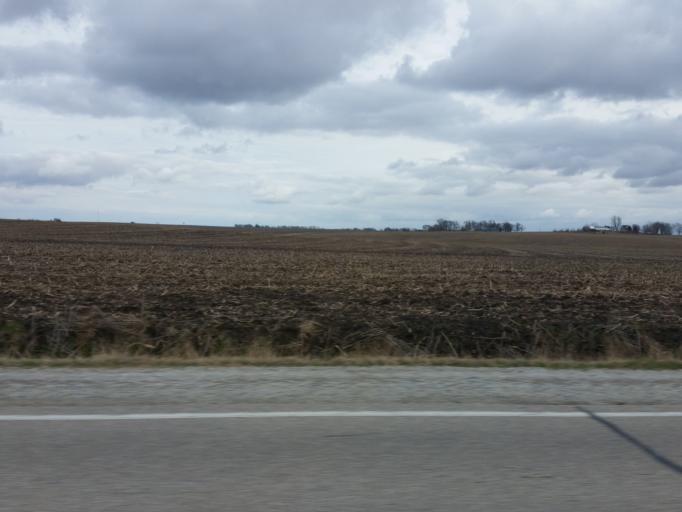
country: US
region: Iowa
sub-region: Black Hawk County
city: Elk Run Heights
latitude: 42.5602
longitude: -92.2193
